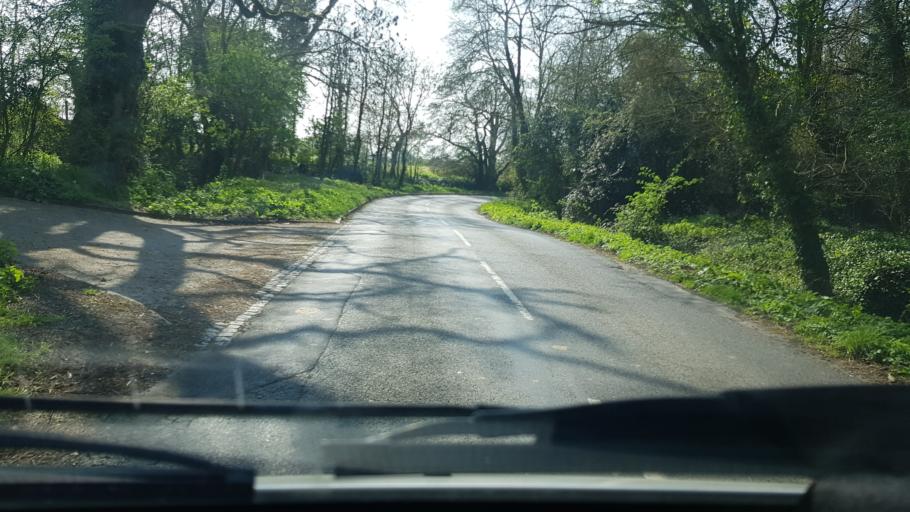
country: GB
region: England
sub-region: West Sussex
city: Chichester
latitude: 50.8230
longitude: -0.8033
